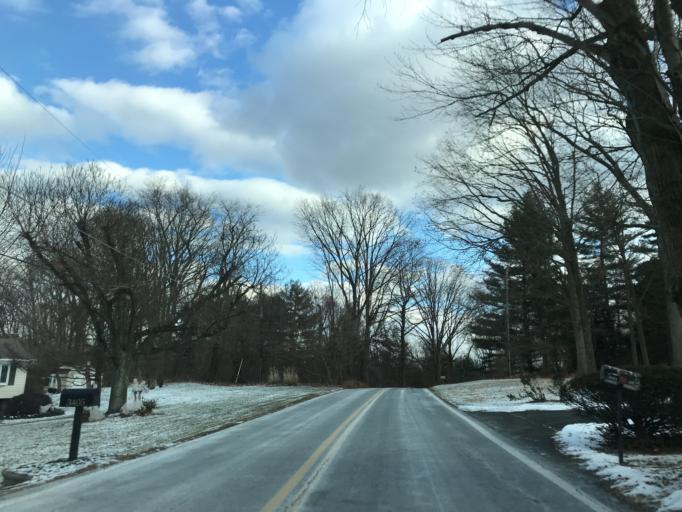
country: US
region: Maryland
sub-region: Harford County
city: Bel Air North
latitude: 39.6386
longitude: -76.3785
